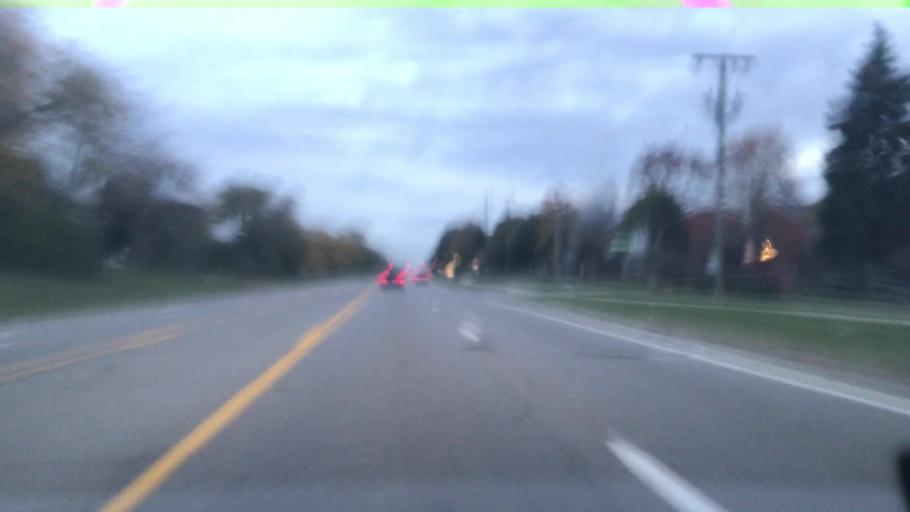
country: US
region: Michigan
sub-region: Oakland County
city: Bloomfield Hills
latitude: 42.6096
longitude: -83.2481
